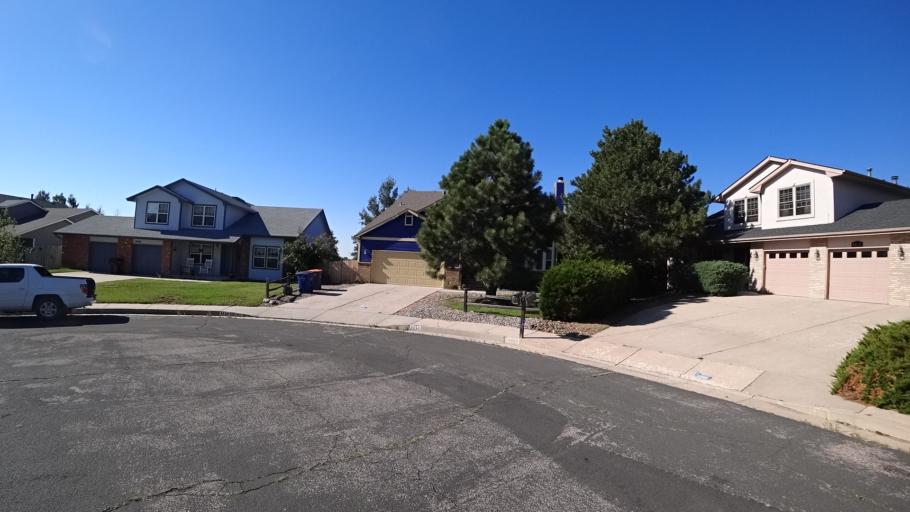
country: US
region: Colorado
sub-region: El Paso County
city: Black Forest
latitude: 38.9576
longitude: -104.7560
